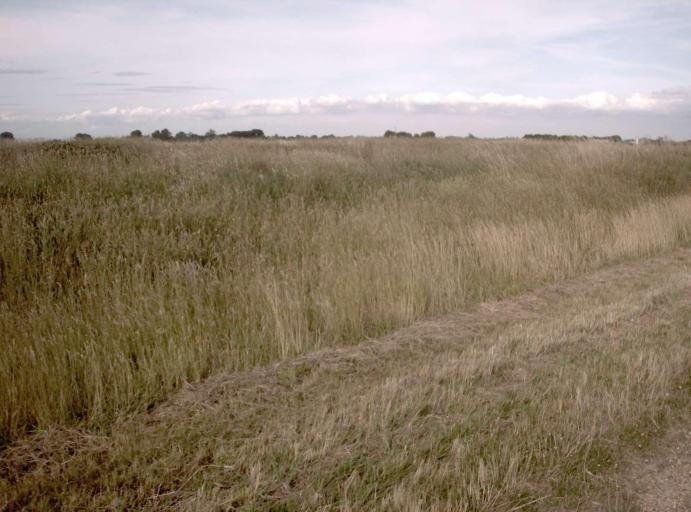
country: AU
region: Victoria
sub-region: Wellington
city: Heyfield
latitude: -38.0194
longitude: 146.7450
